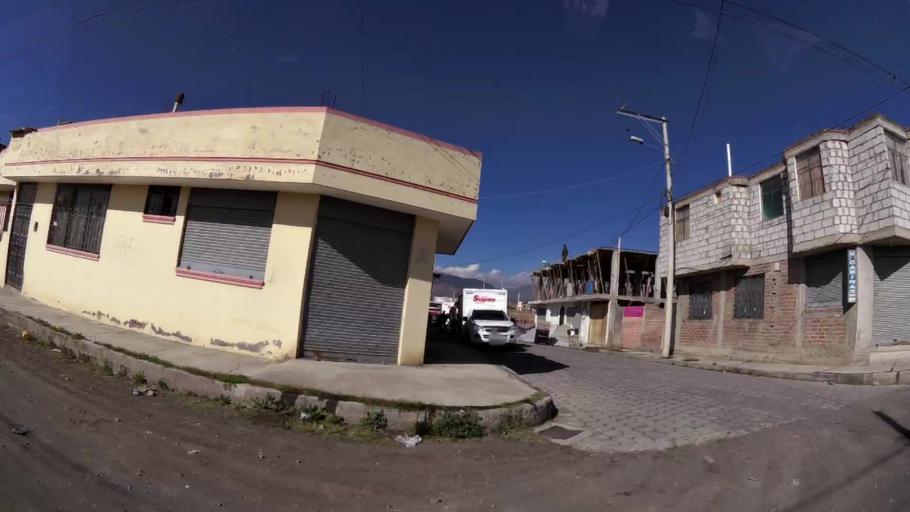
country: EC
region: Chimborazo
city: Riobamba
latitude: -1.6499
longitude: -78.6749
